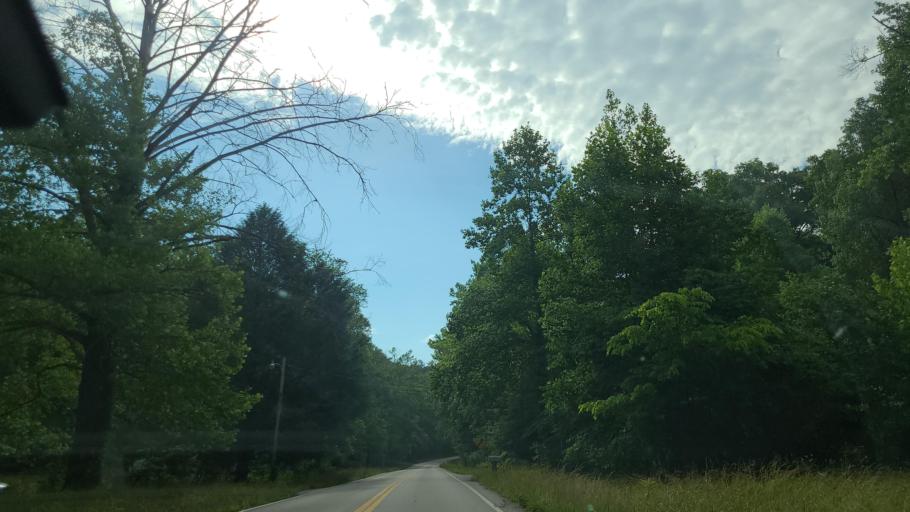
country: US
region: Kentucky
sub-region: Knox County
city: Barbourville
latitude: 36.6810
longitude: -83.9107
